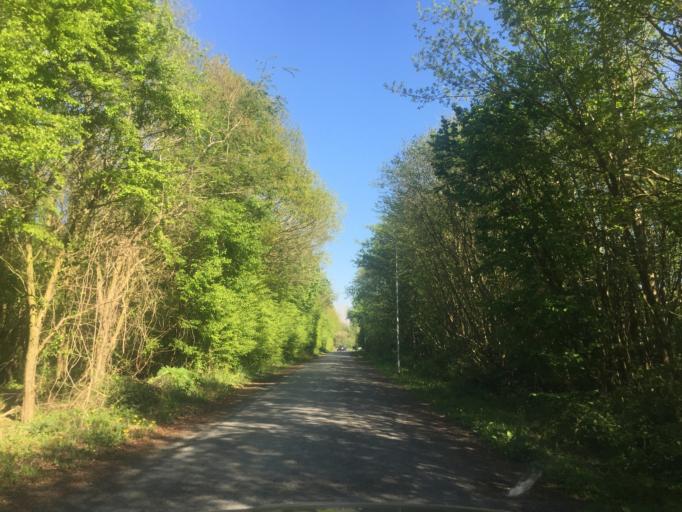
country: DK
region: South Denmark
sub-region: Odense Kommune
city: Odense
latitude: 55.3708
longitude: 10.4032
